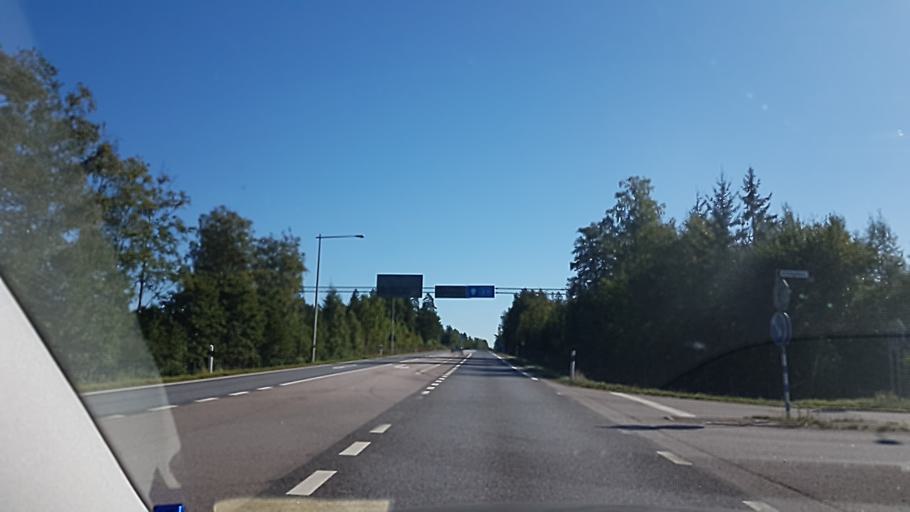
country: SE
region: Kronoberg
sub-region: Vaxjo Kommun
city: Vaexjoe
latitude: 56.8838
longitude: 14.8530
